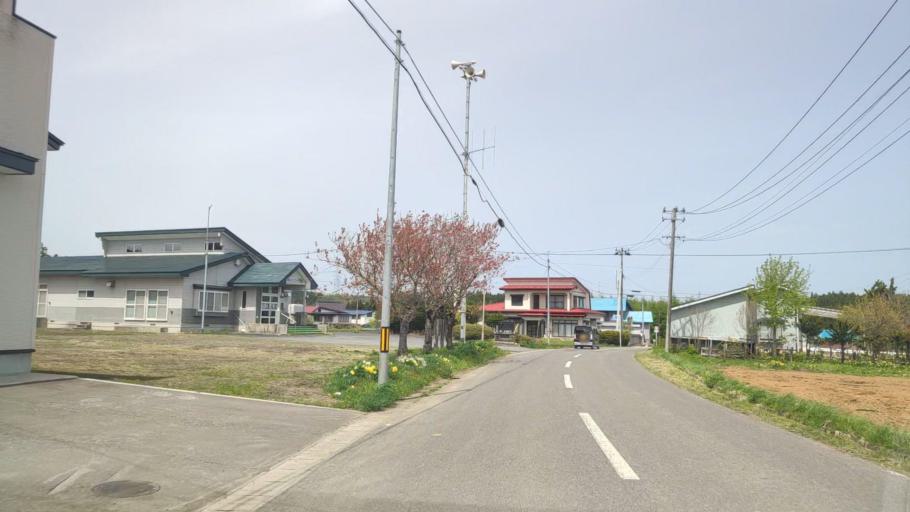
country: JP
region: Aomori
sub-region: Misawa Shi
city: Inuotose
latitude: 40.7776
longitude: 141.1223
